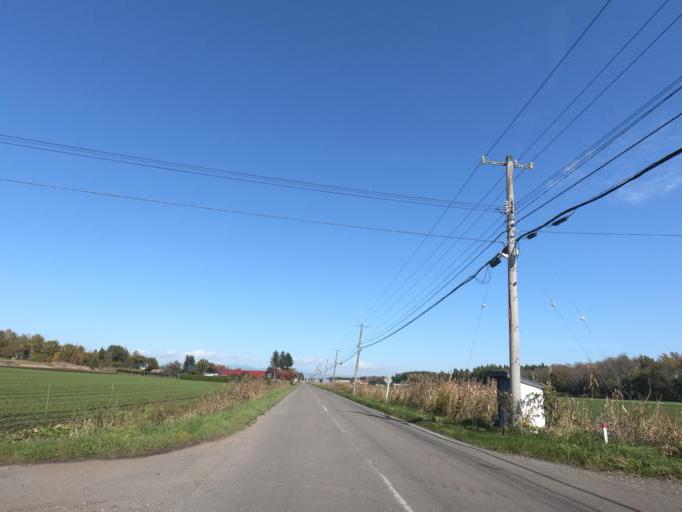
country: JP
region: Hokkaido
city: Obihiro
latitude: 42.9539
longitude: 143.2285
